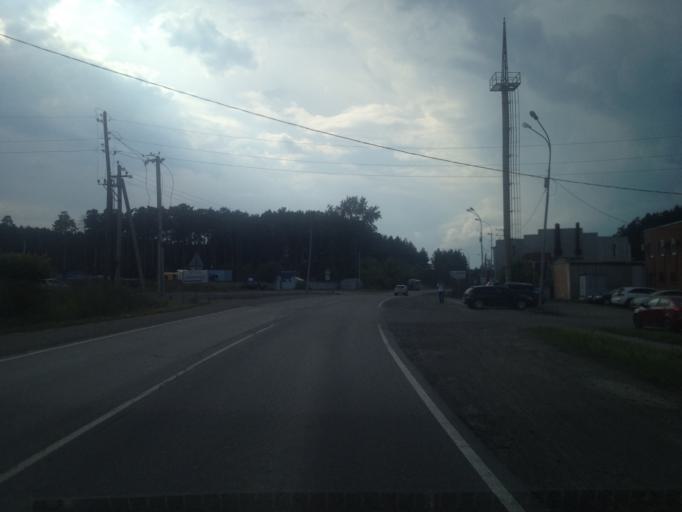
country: RU
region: Sverdlovsk
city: Shirokaya Rechka
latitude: 56.8173
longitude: 60.5142
